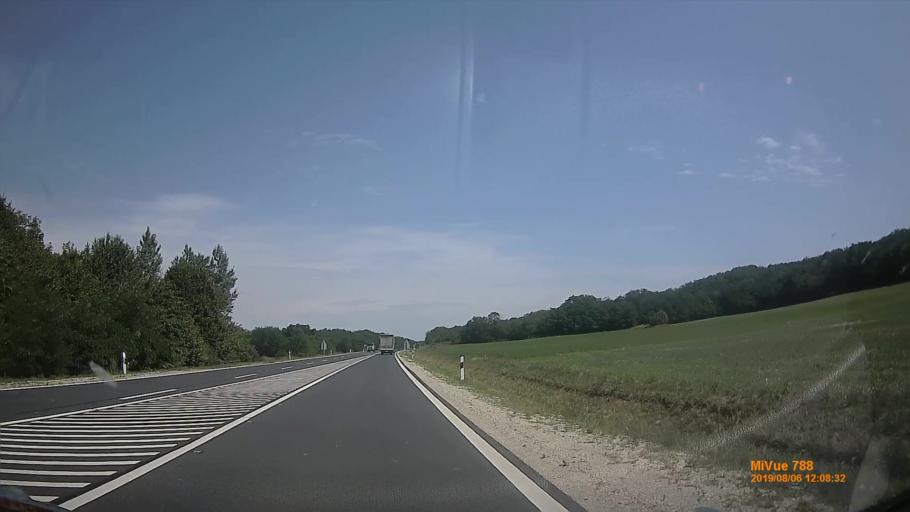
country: HU
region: Vas
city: Vasvar
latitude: 47.0892
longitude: 16.8647
